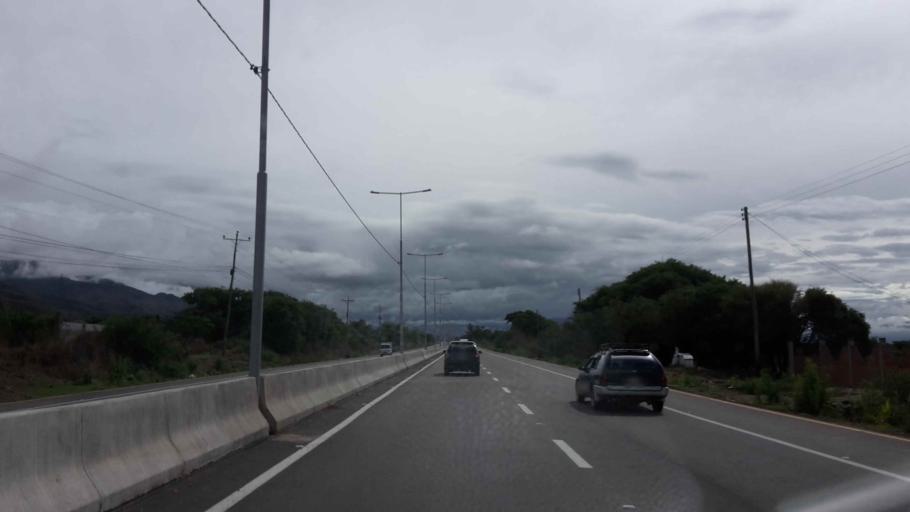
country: BO
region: Cochabamba
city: Tarata
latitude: -17.5441
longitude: -66.0031
